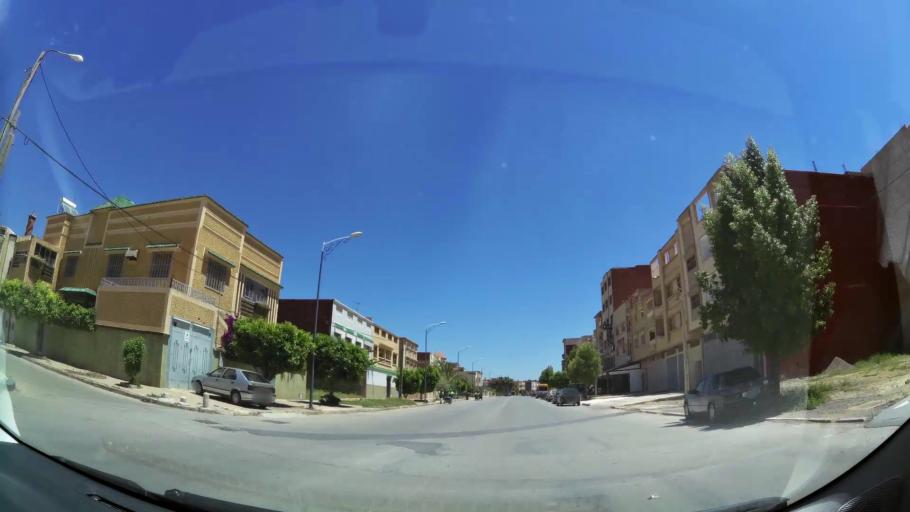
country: MA
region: Oriental
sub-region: Oujda-Angad
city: Oujda
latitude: 34.6761
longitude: -1.8780
